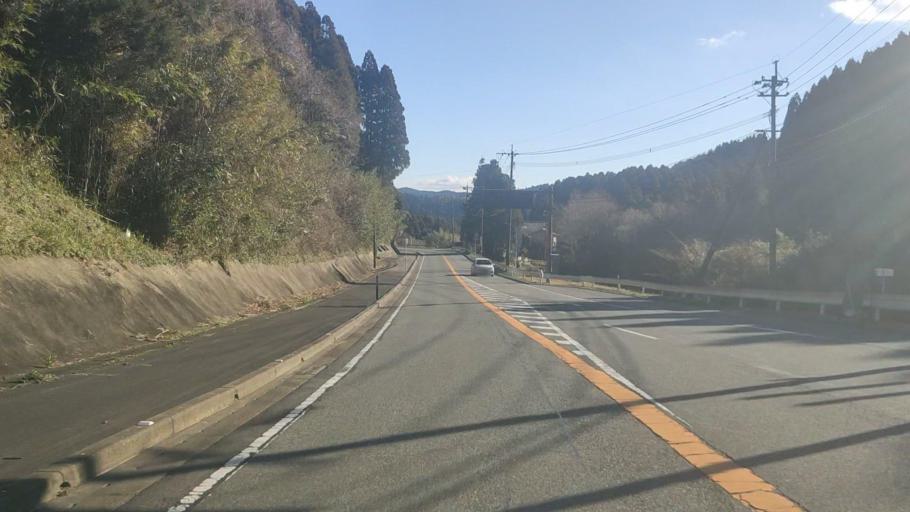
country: JP
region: Fukuoka
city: Maebaru-chuo
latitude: 33.4583
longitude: 130.2738
